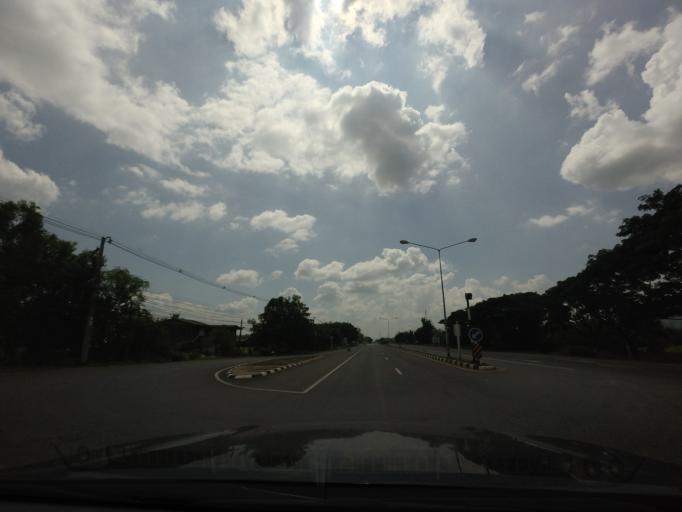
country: TH
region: Phetchabun
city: Nong Phai
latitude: 16.1659
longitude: 101.0737
